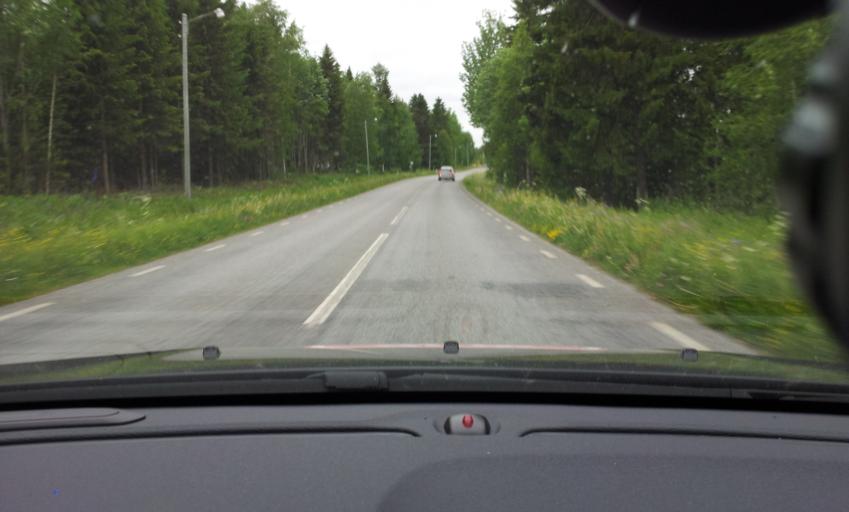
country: SE
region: Jaemtland
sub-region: Krokoms Kommun
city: Krokom
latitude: 63.1514
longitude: 14.1587
